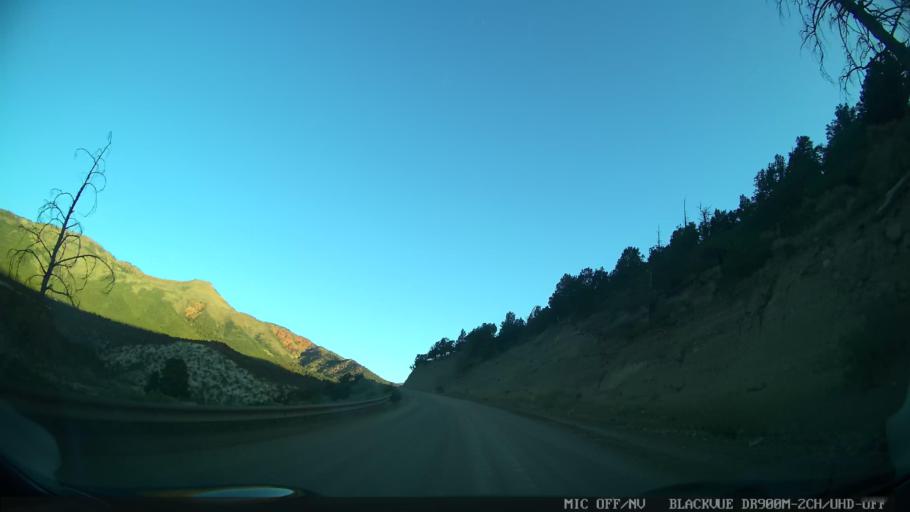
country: US
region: Colorado
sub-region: Eagle County
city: Edwards
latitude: 39.8963
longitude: -106.6067
